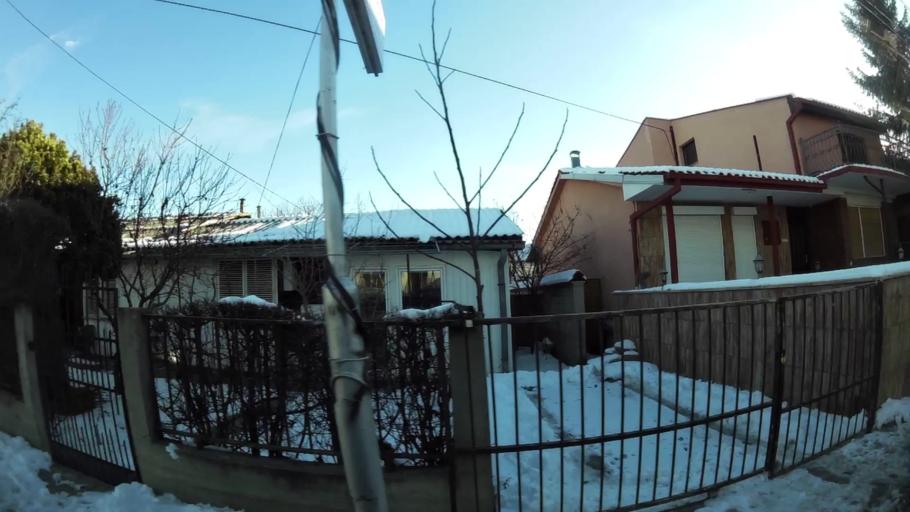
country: MK
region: Saraj
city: Saraj
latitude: 42.0088
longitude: 21.3334
